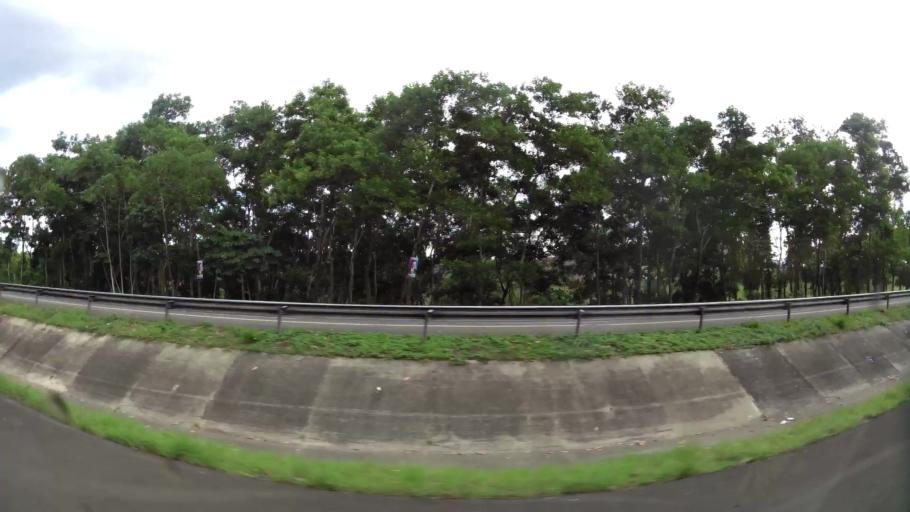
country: DO
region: Monsenor Nouel
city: Bonao
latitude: 18.9195
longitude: -70.3809
